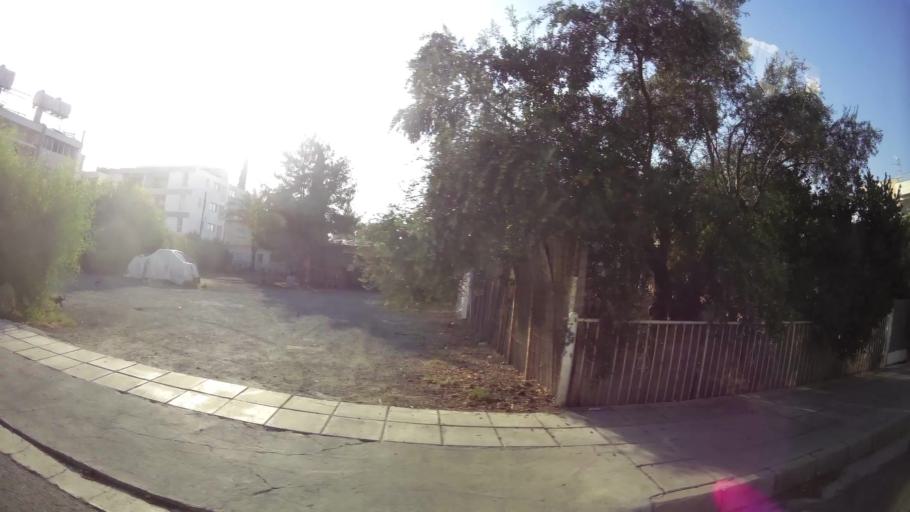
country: CY
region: Lefkosia
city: Nicosia
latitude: 35.1748
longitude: 33.3407
